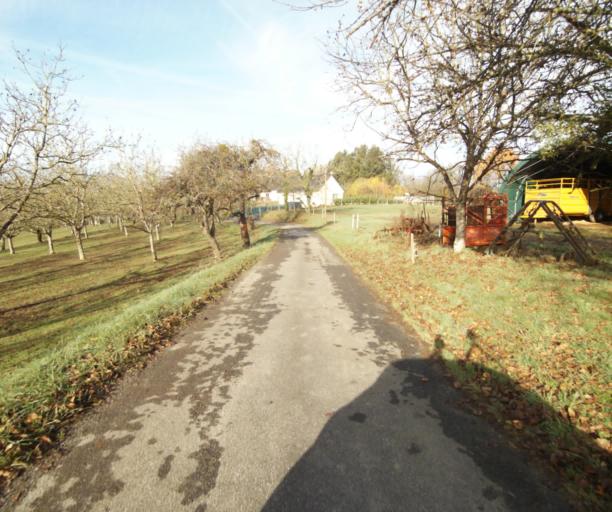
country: FR
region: Limousin
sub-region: Departement de la Correze
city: Sainte-Fortunade
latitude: 45.2250
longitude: 1.7384
